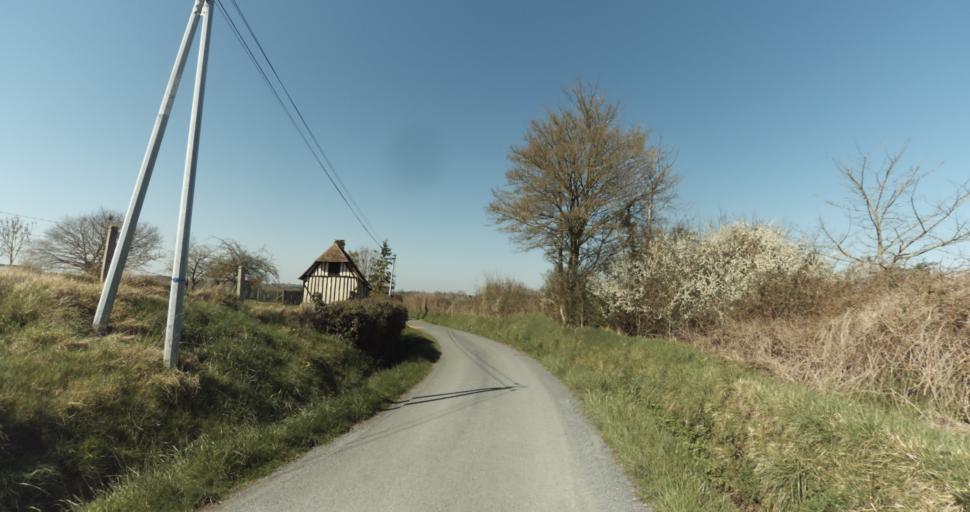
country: FR
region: Lower Normandy
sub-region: Departement du Calvados
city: Saint-Pierre-sur-Dives
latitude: 49.0079
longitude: 0.0300
